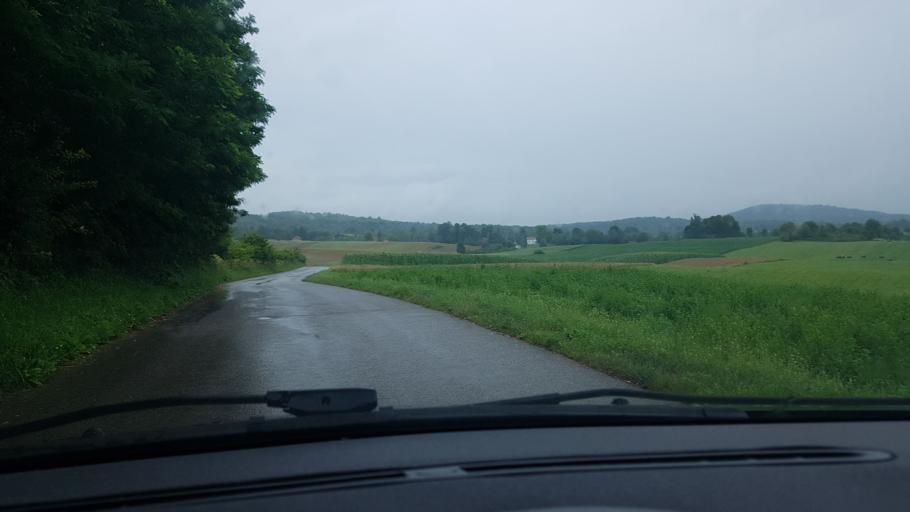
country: HR
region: Licko-Senjska
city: Jezerce
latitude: 44.9895
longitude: 15.6682
